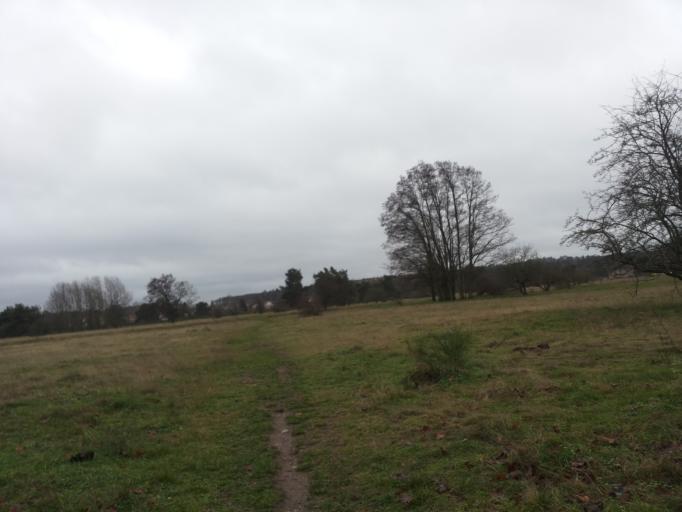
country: DE
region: Bavaria
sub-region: Regierungsbezirk Mittelfranken
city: Wendelstein
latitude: 49.4028
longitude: 11.1678
